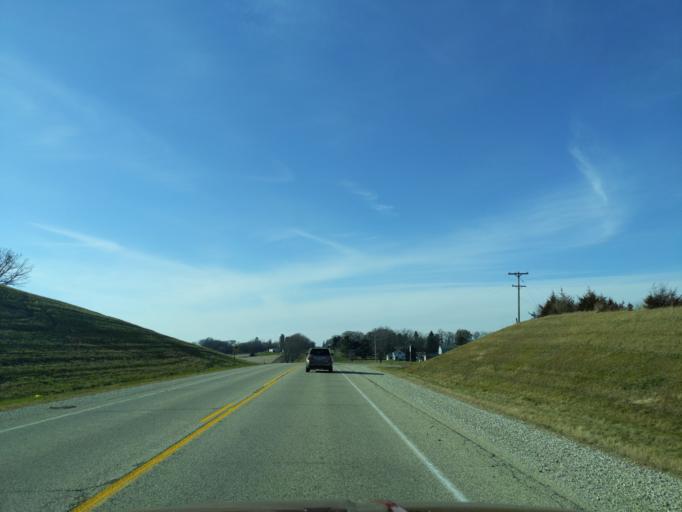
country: US
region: Wisconsin
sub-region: Jefferson County
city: Fort Atkinson
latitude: 42.8289
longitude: -88.8357
